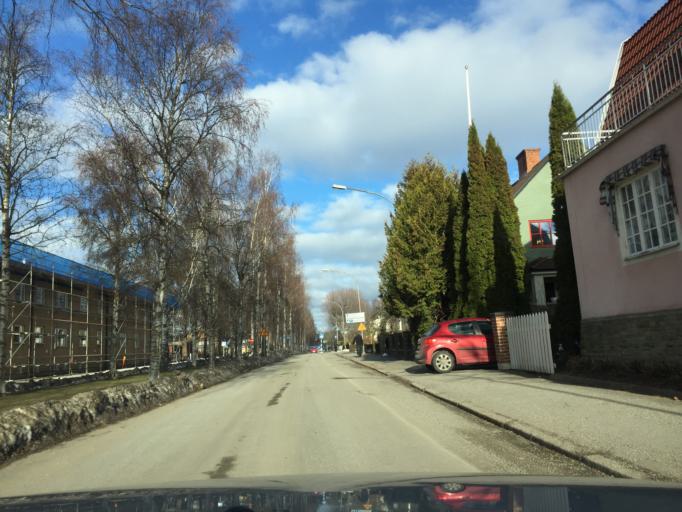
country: SE
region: OErebro
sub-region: Orebro Kommun
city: Orebro
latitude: 59.2697
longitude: 15.2358
